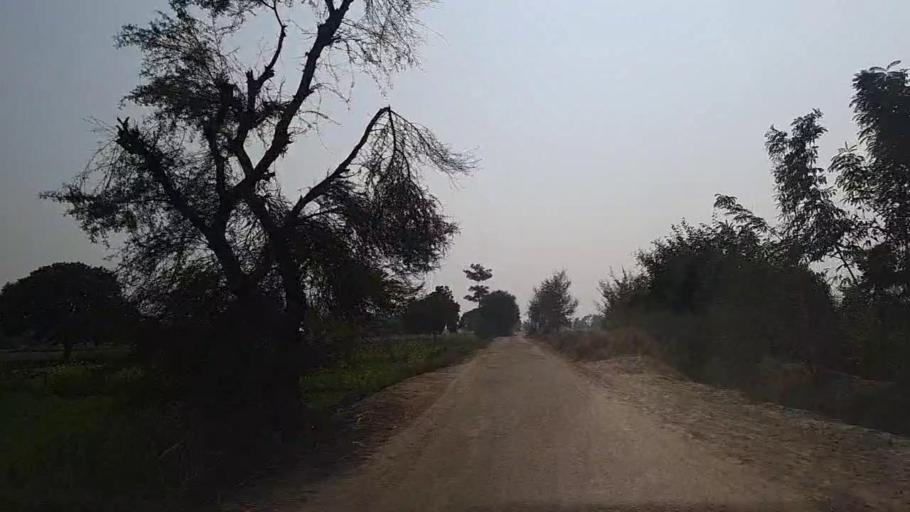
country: PK
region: Sindh
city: Jam Sahib
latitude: 26.4611
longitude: 68.5236
